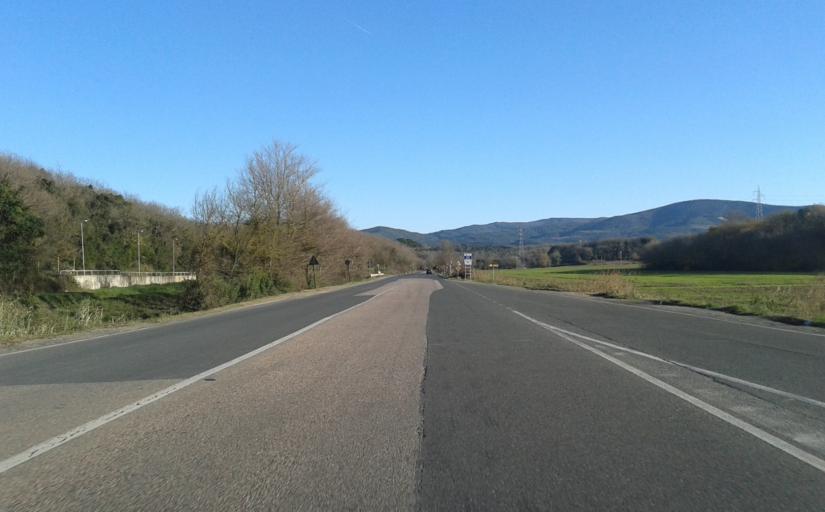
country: IT
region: Tuscany
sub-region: Provincia di Livorno
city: Livorno
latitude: 43.5716
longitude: 10.3523
